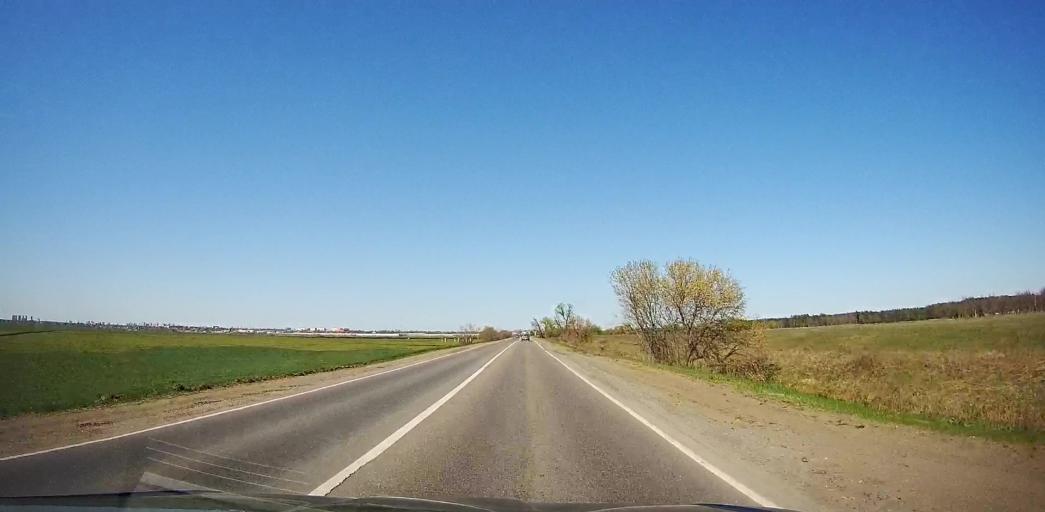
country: RU
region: Moskovskaya
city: Ramenskoye
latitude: 55.5217
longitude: 38.2765
